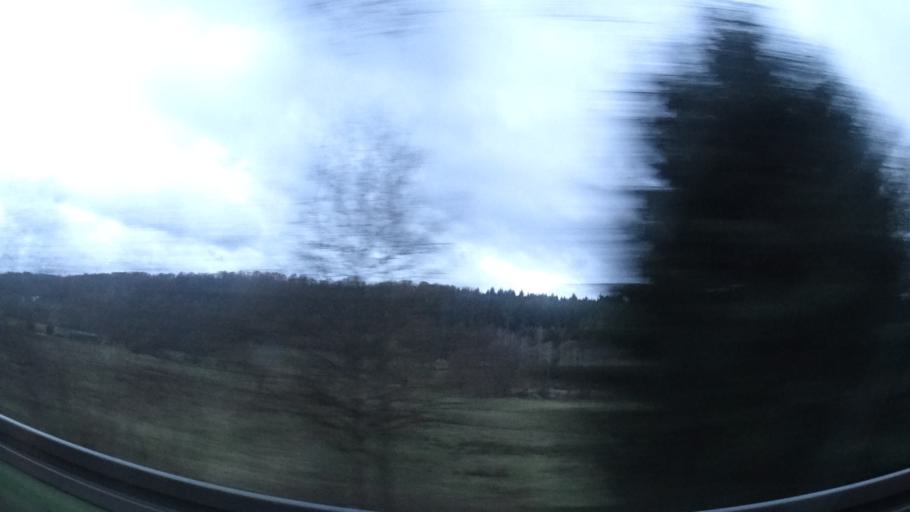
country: DE
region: Hesse
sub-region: Regierungsbezirk Kassel
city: Eichenzell
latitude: 50.4475
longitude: 9.7309
